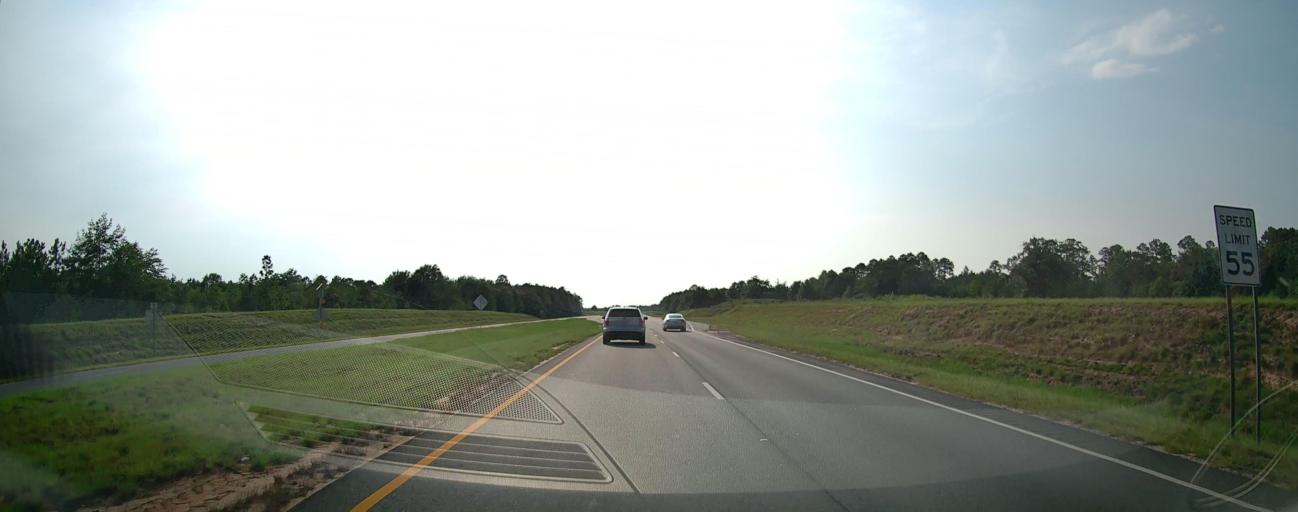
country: US
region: Georgia
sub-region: Taylor County
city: Butler
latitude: 32.5451
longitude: -84.2442
